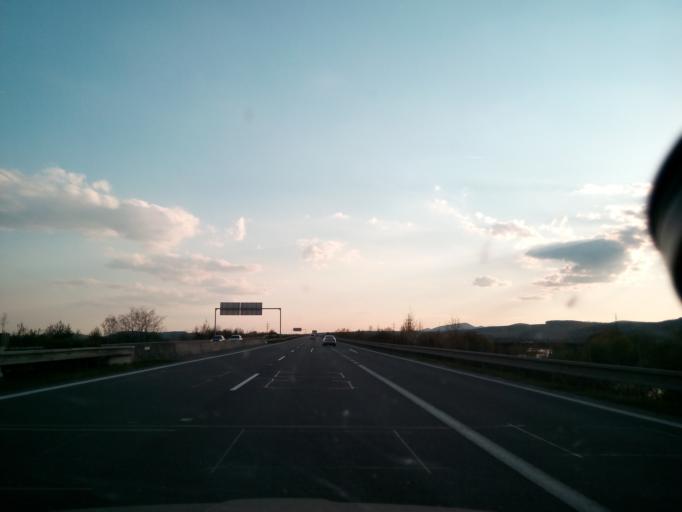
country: SK
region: Nitriansky
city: Nemsova
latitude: 48.9607
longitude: 18.1328
